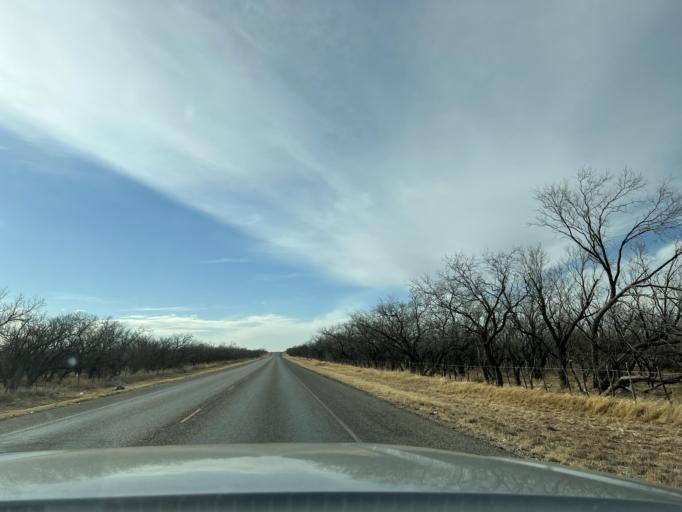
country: US
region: Texas
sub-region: Fisher County
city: Rotan
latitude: 32.7397
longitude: -100.5183
